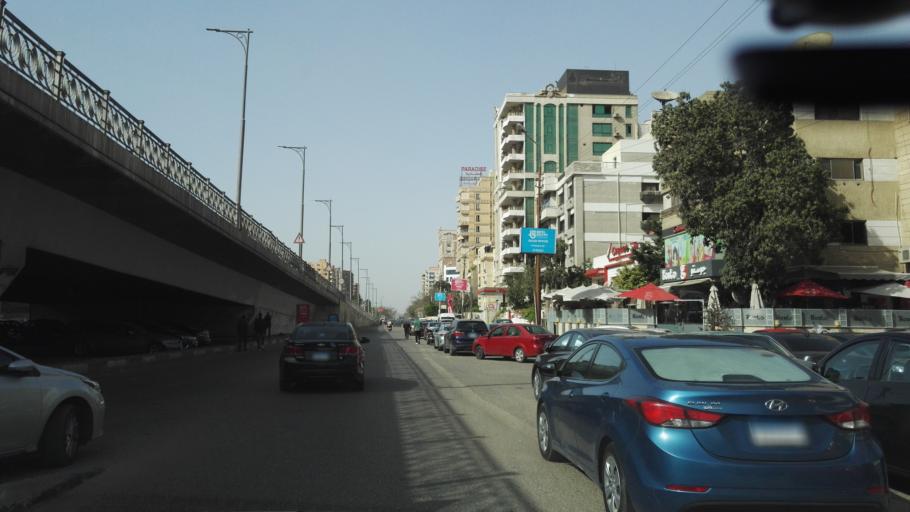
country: EG
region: Muhafazat al Qahirah
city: Cairo
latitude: 30.0843
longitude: 31.3408
